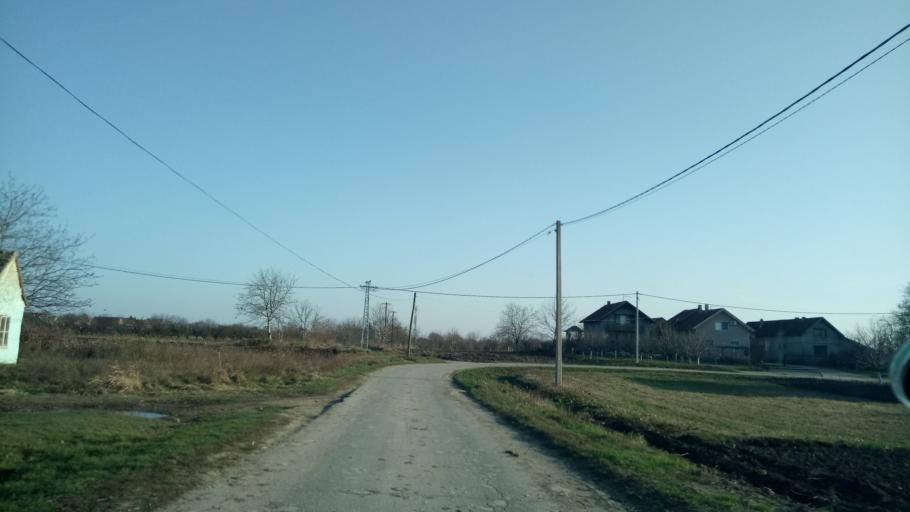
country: RS
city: Novi Slankamen
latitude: 45.1311
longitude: 20.2315
